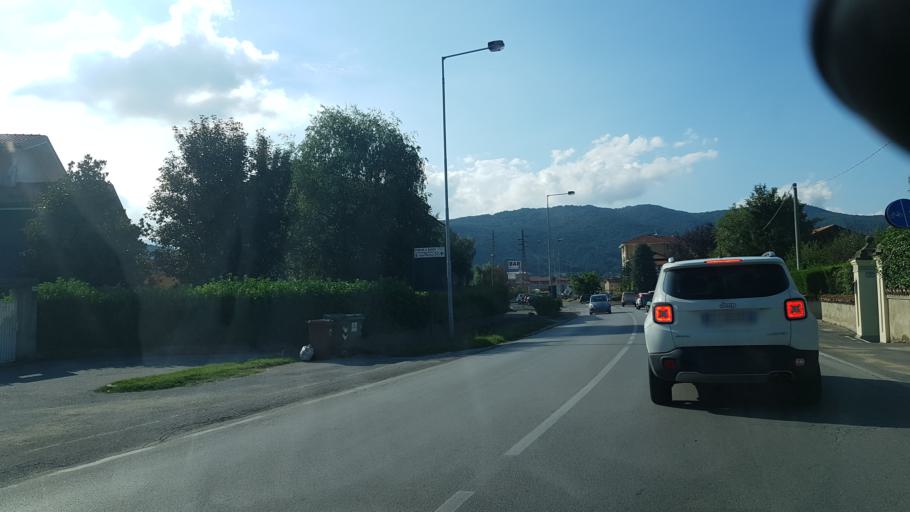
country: IT
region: Piedmont
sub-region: Provincia di Cuneo
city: Busca
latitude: 44.5096
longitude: 7.4852
